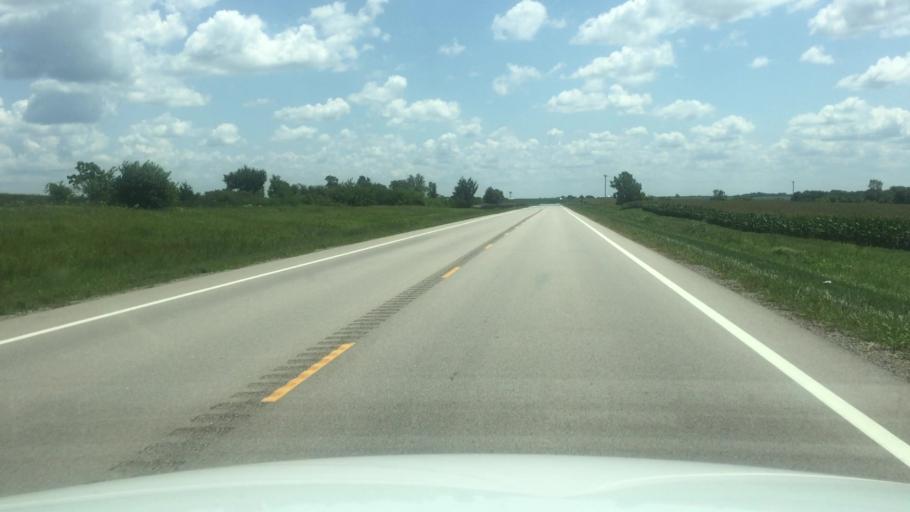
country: US
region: Kansas
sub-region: Brown County
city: Horton
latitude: 39.5976
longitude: -95.3346
